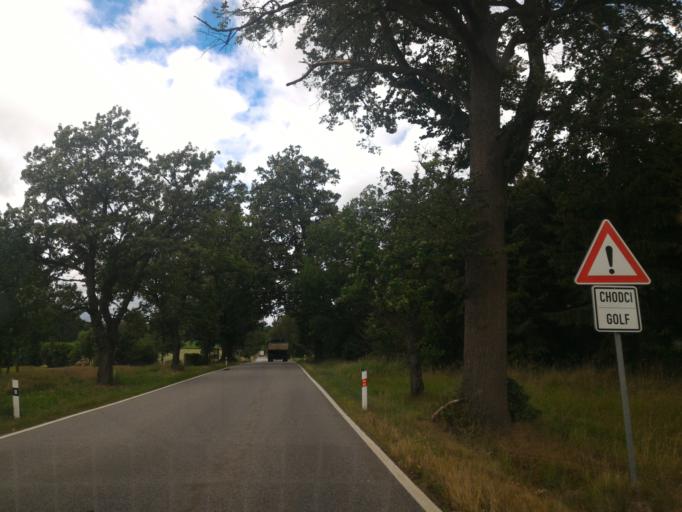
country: CZ
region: Vysocina
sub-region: Okres Jihlava
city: Telc
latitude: 49.2127
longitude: 15.4304
